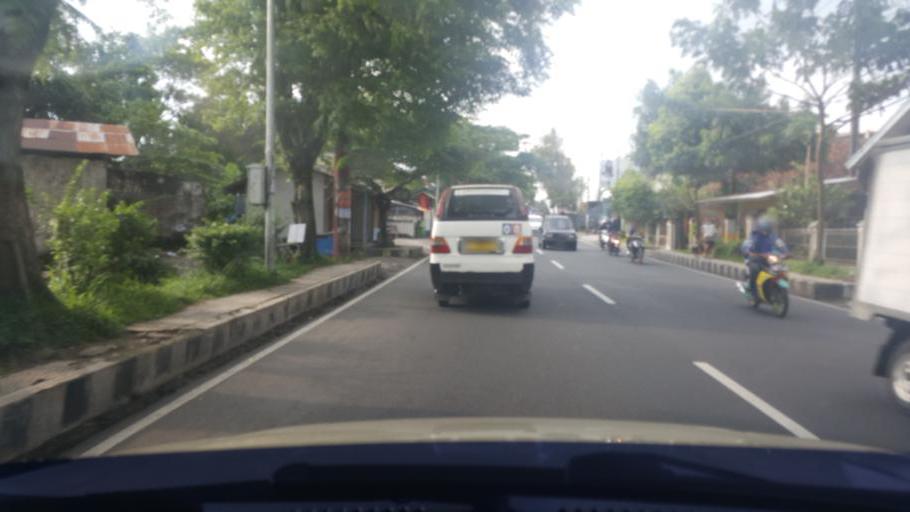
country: ID
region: West Java
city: Gunungbatu
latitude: -7.3113
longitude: 108.2107
